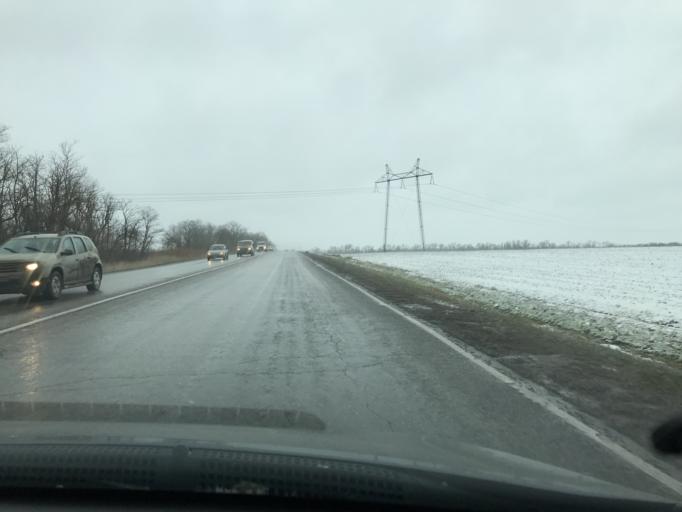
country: RU
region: Rostov
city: Zernograd
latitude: 46.8260
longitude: 40.2481
